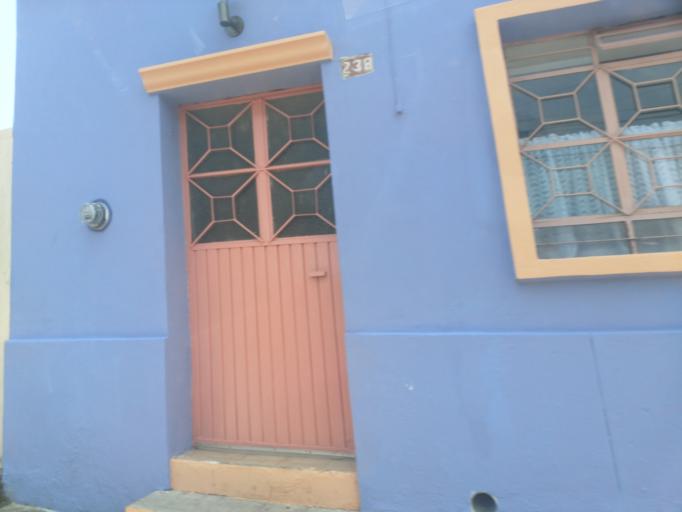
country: MX
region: Nayarit
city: Tepic
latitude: 21.5096
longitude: -104.8873
